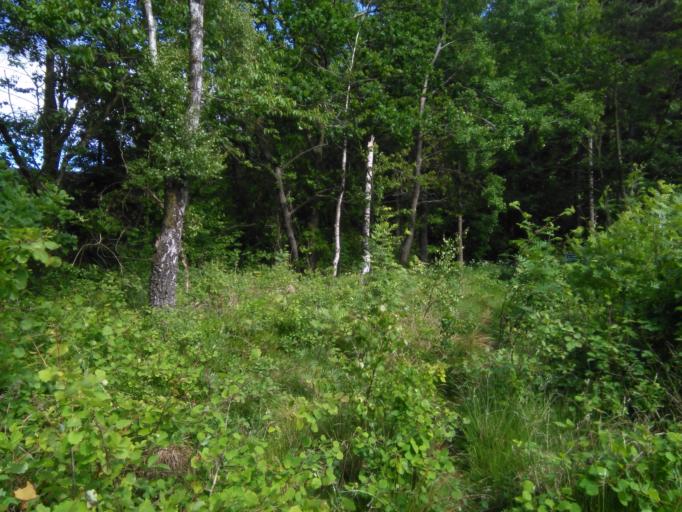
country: DK
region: Capital Region
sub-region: Bornholm Kommune
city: Nexo
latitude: 55.0933
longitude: 15.1088
